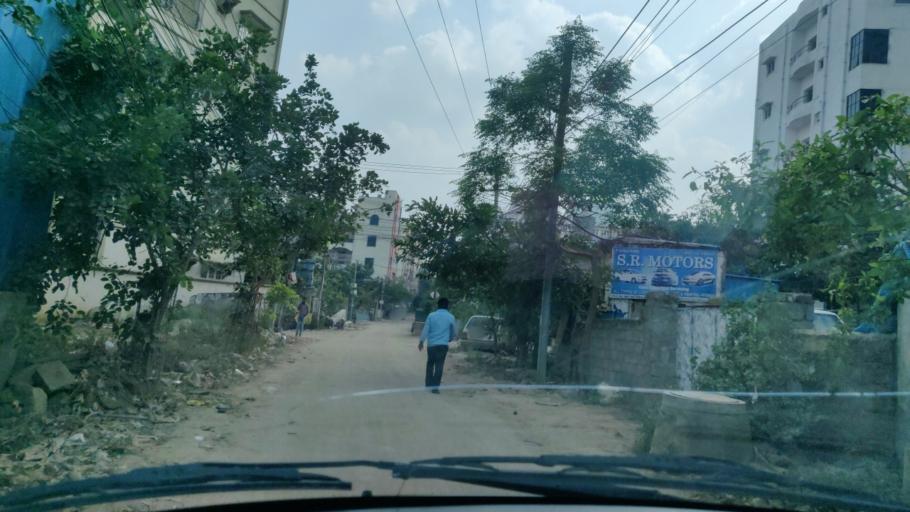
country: IN
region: Telangana
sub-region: Rangareddi
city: Kukatpalli
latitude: 17.4509
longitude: 78.3941
